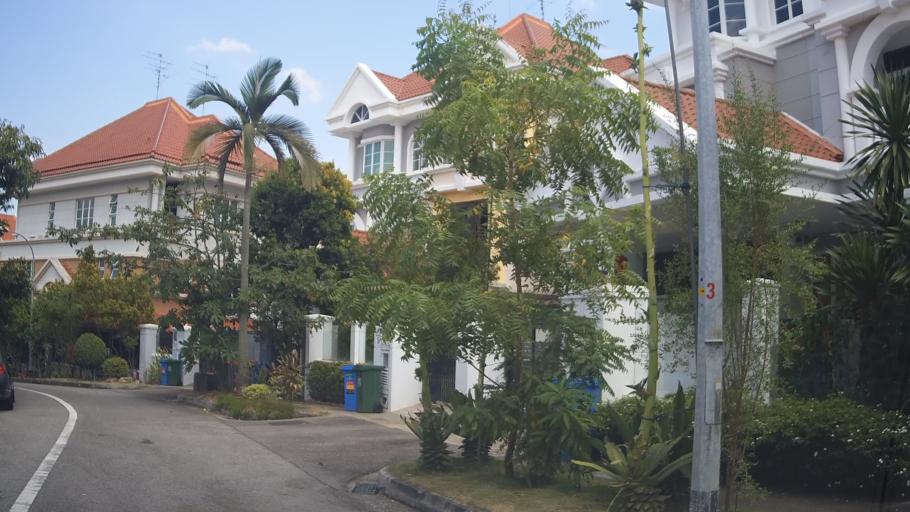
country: SG
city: Singapore
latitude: 1.3203
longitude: 103.9492
